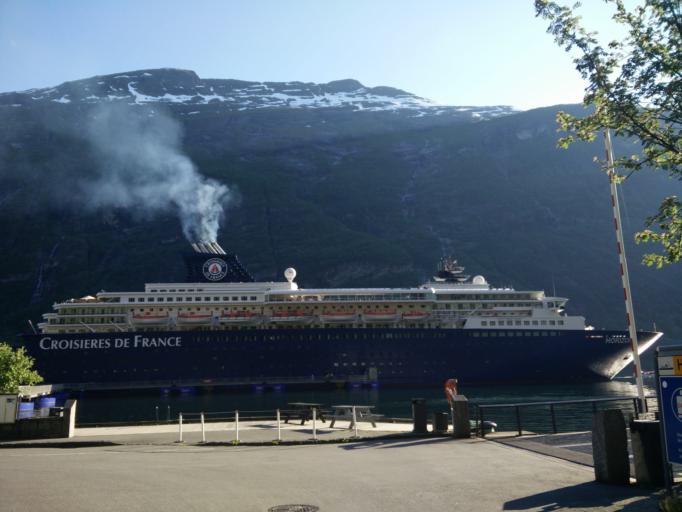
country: NO
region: More og Romsdal
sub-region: Norddal
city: Valldal
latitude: 62.1037
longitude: 7.2032
